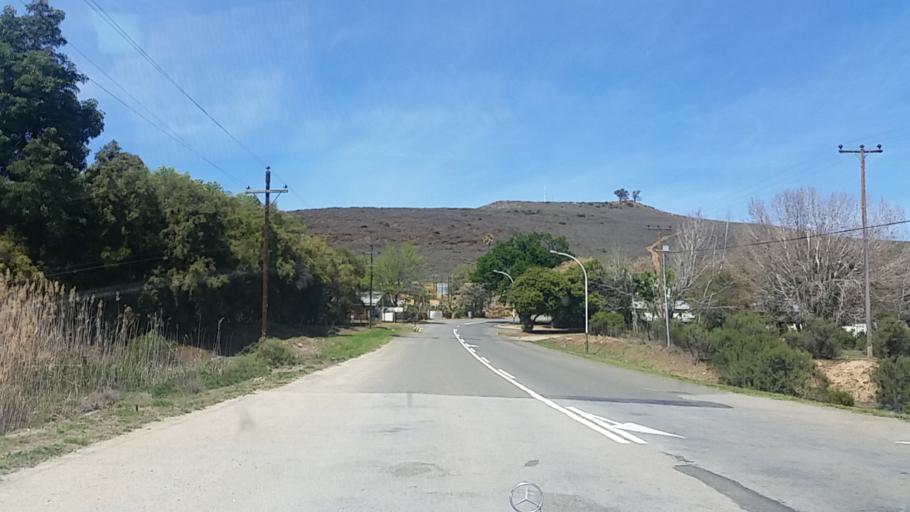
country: ZA
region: Western Cape
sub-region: Eden District Municipality
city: Knysna
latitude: -33.6539
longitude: 23.1348
